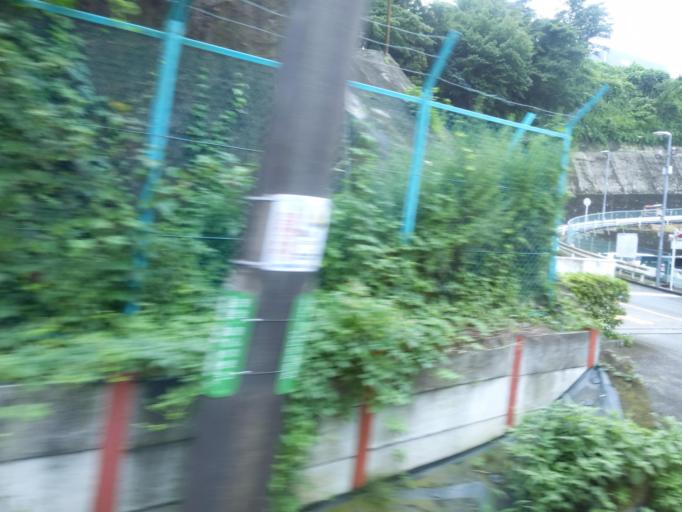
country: JP
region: Tokyo
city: Chofugaoka
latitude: 35.6090
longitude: 139.6009
